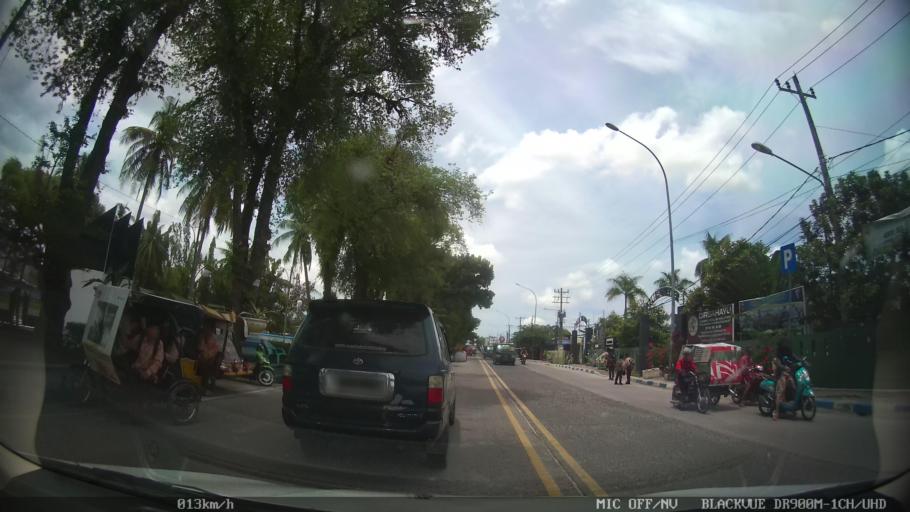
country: ID
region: North Sumatra
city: Percut
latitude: 3.5587
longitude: 98.8799
